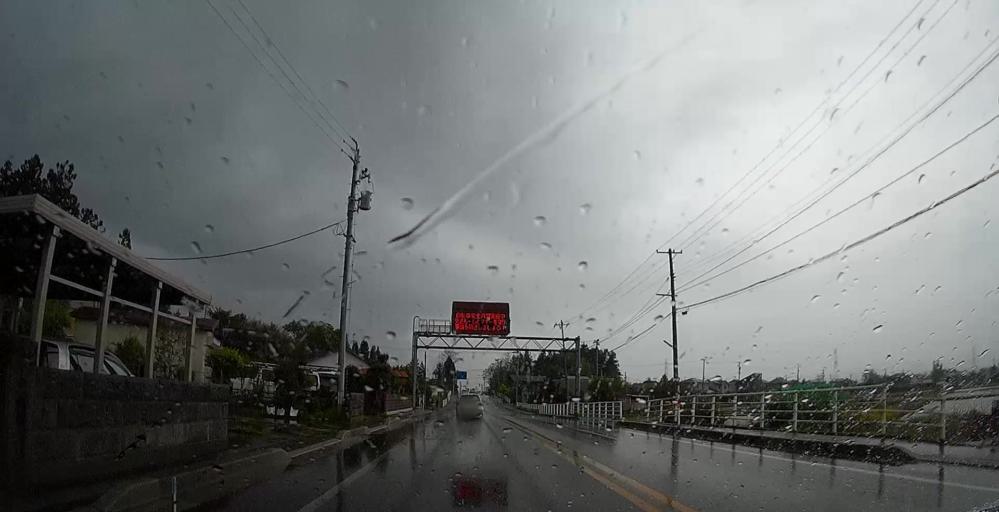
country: JP
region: Niigata
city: Kashiwazaki
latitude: 37.3944
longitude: 138.6024
